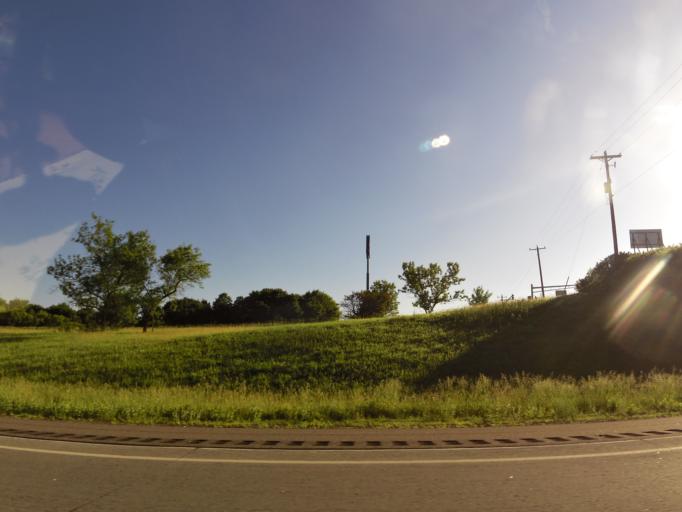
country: US
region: Minnesota
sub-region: Wright County
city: Clearwater
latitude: 45.4122
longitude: -94.0576
